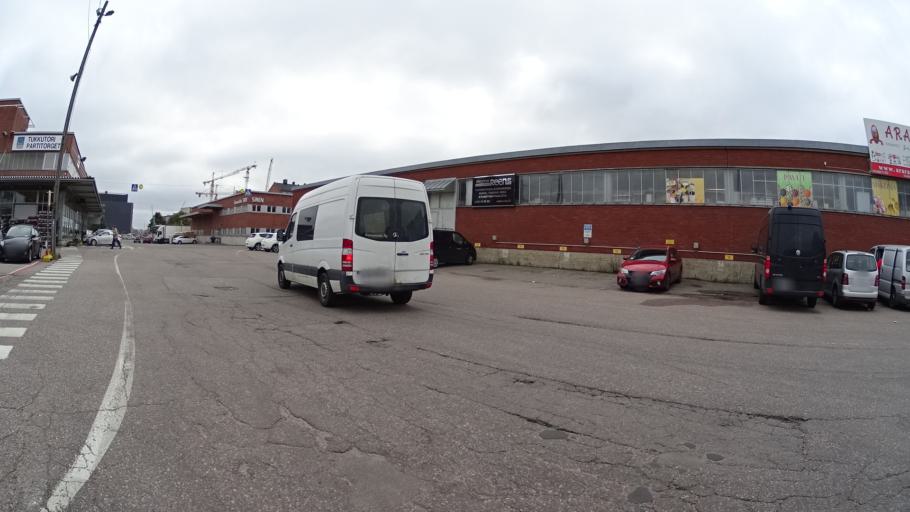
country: FI
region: Uusimaa
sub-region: Helsinki
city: Helsinki
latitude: 60.1910
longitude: 24.9731
